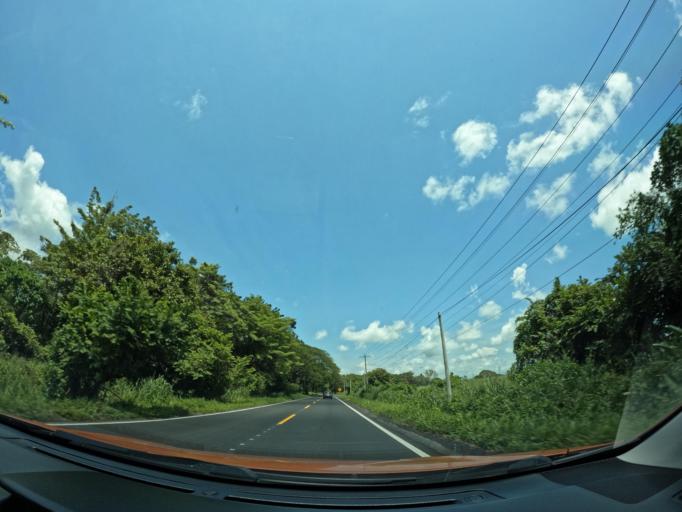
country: GT
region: Escuintla
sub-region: Municipio de Masagua
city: Masagua
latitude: 14.1800
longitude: -90.8669
